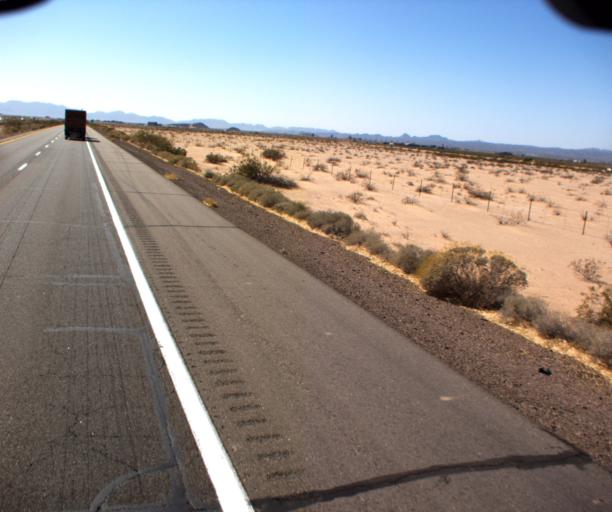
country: US
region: Arizona
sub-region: Yuma County
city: Wellton
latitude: 32.6862
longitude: -114.0009
